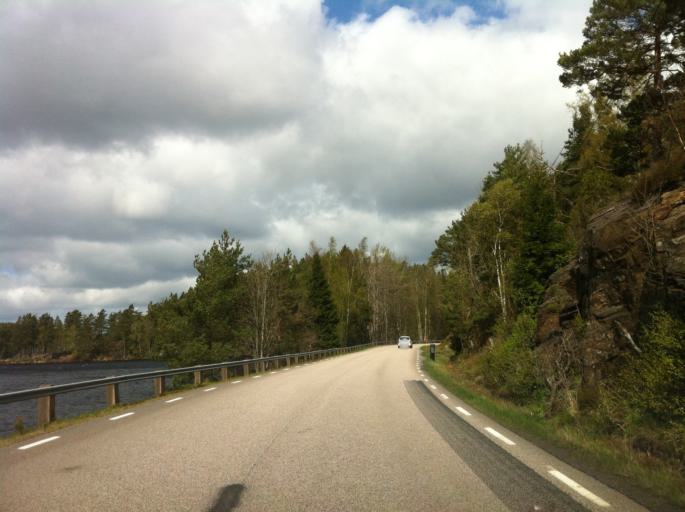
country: SE
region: Vaestra Goetaland
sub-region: Alingsas Kommun
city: Ingared
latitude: 57.8307
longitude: 12.5553
